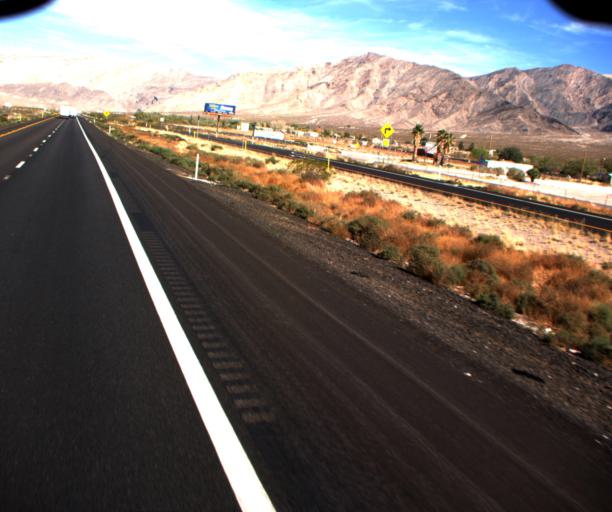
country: US
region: Arizona
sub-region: Mohave County
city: Beaver Dam
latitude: 36.8963
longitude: -113.9092
